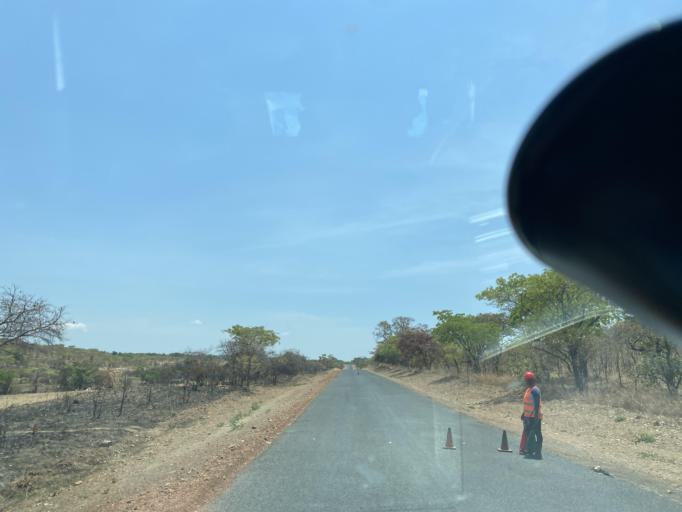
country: ZM
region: Lusaka
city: Kafue
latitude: -15.8417
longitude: 28.4094
